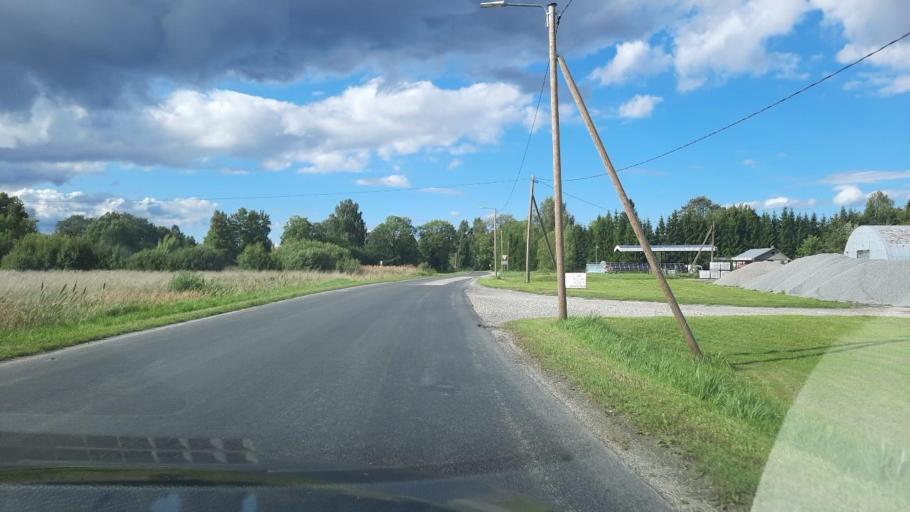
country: EE
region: Paernumaa
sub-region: Tootsi vald
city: Tootsi
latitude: 58.4900
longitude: 24.8978
